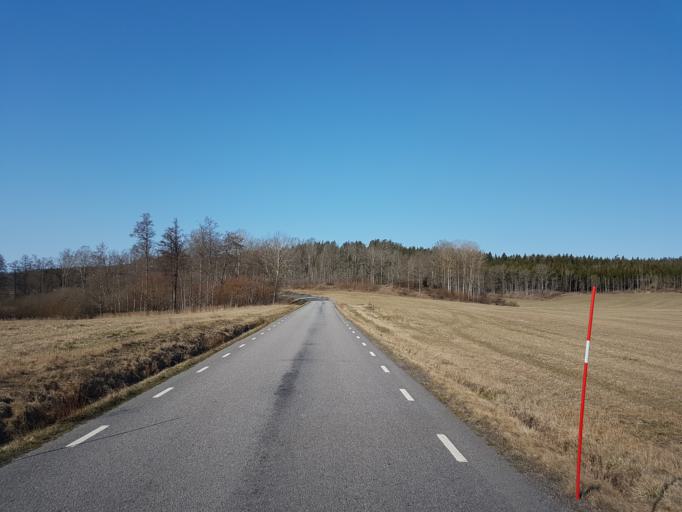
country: SE
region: OEstergoetland
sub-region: Valdemarsviks Kommun
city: Gusum
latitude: 58.2003
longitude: 16.3482
